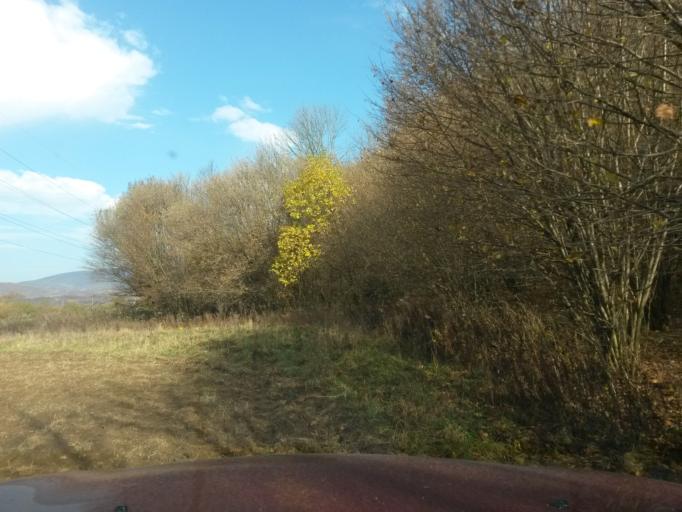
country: SK
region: Kosicky
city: Roznava
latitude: 48.6039
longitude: 20.4848
